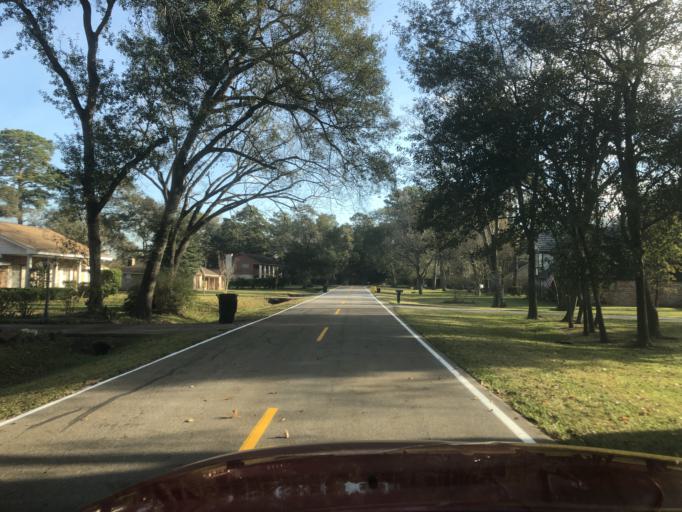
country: US
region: Texas
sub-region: Harris County
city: Spring
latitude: 30.0158
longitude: -95.4732
